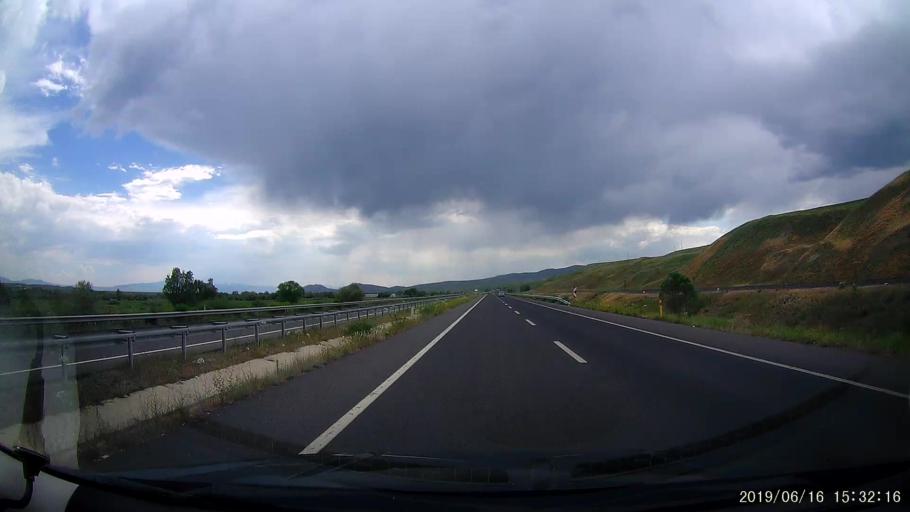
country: TR
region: Erzurum
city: Horasan
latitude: 40.0300
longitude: 42.0529
